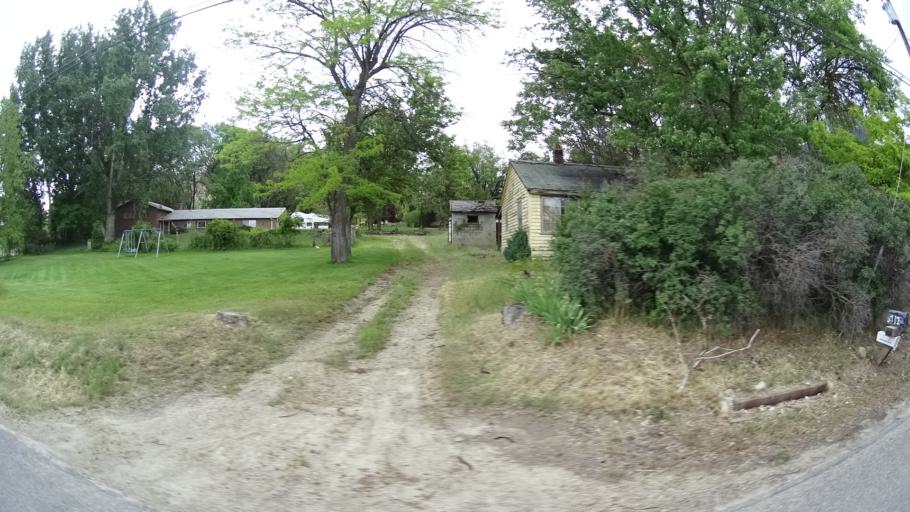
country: US
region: Idaho
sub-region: Ada County
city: Garden City
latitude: 43.6740
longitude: -116.2597
